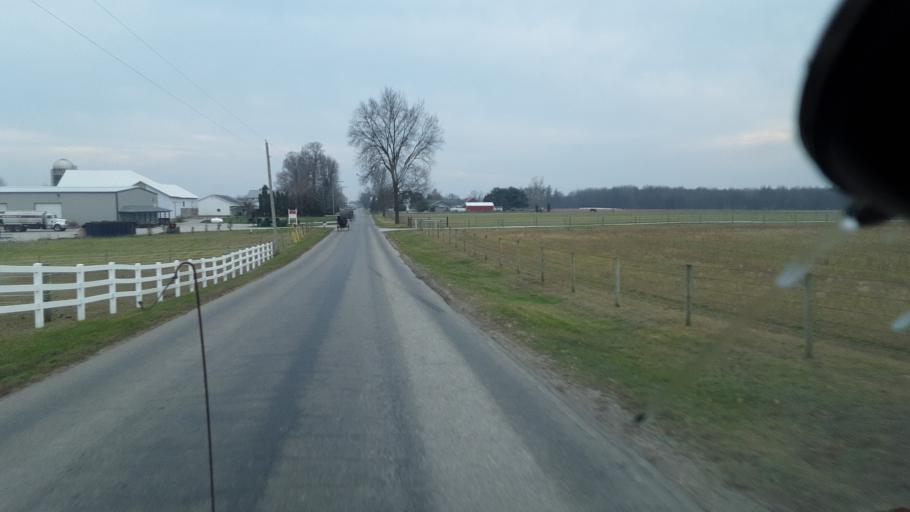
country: US
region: Indiana
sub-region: Elkhart County
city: Middlebury
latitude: 41.7000
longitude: -85.6201
